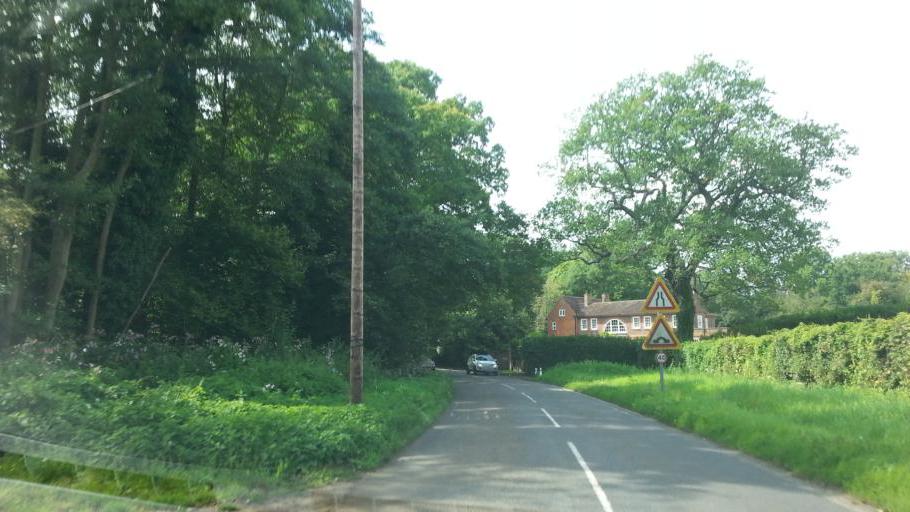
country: GB
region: England
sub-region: Surrey
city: Woking
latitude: 51.3473
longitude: -0.5707
